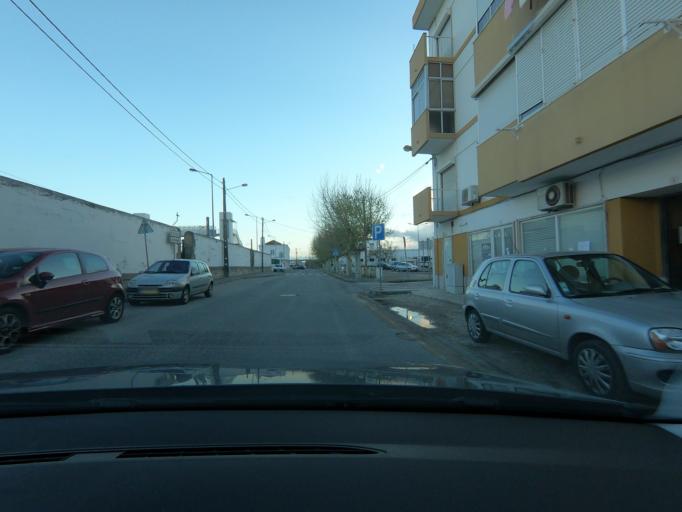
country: PT
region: Lisbon
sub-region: Vila Franca de Xira
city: Castanheira do Ribatejo
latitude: 39.0067
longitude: -8.9534
